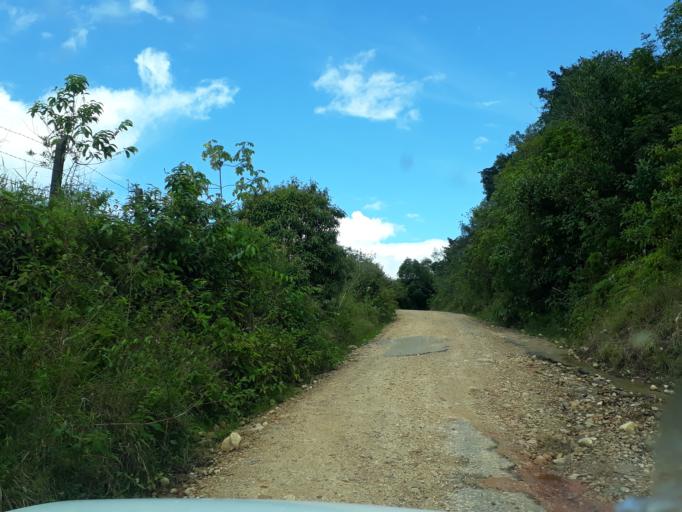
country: CO
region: Cundinamarca
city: Medina
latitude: 4.5916
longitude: -73.3130
